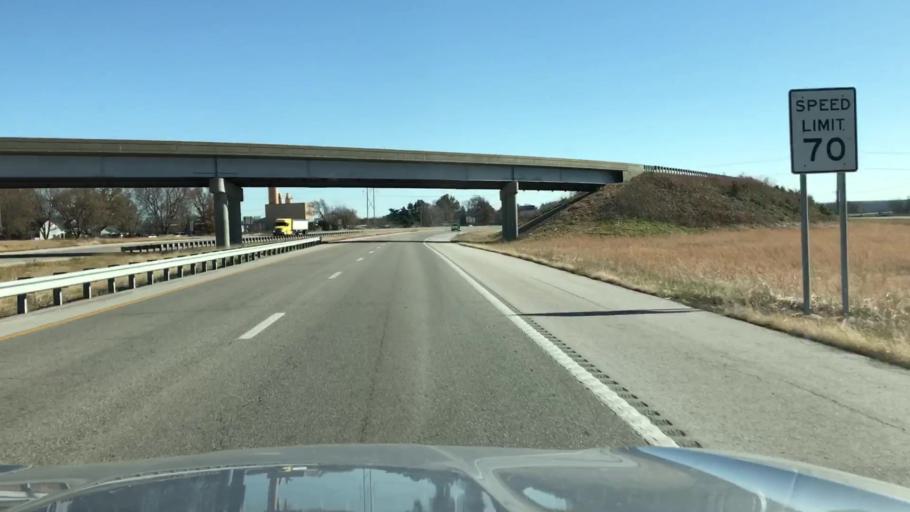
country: US
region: Missouri
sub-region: Jasper County
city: Carthage
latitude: 37.1334
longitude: -94.3144
